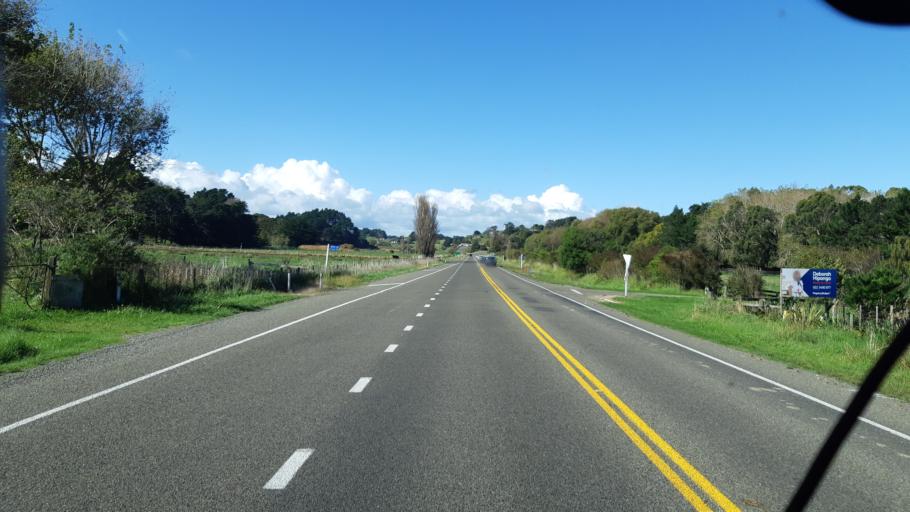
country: NZ
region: Manawatu-Wanganui
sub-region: Wanganui District
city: Wanganui
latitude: -39.9511
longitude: 175.0567
